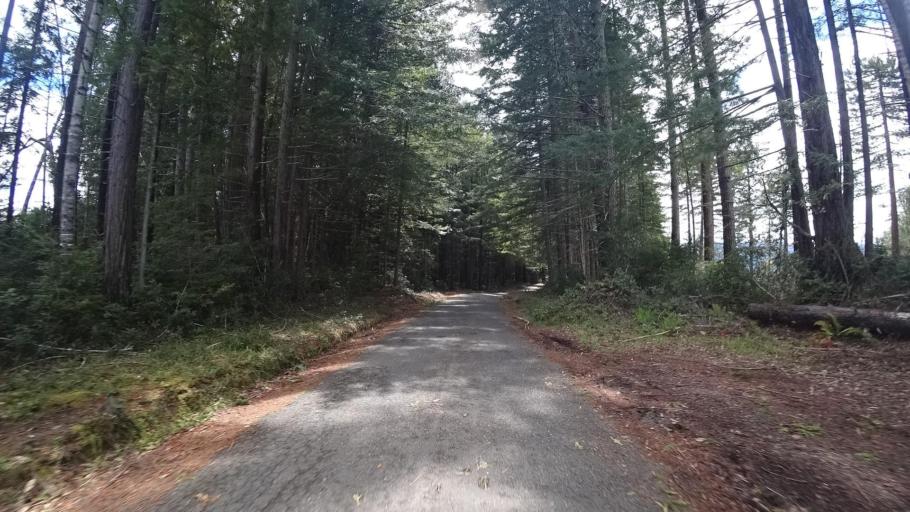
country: US
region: California
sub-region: Humboldt County
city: Blue Lake
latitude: 40.7850
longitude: -123.9640
